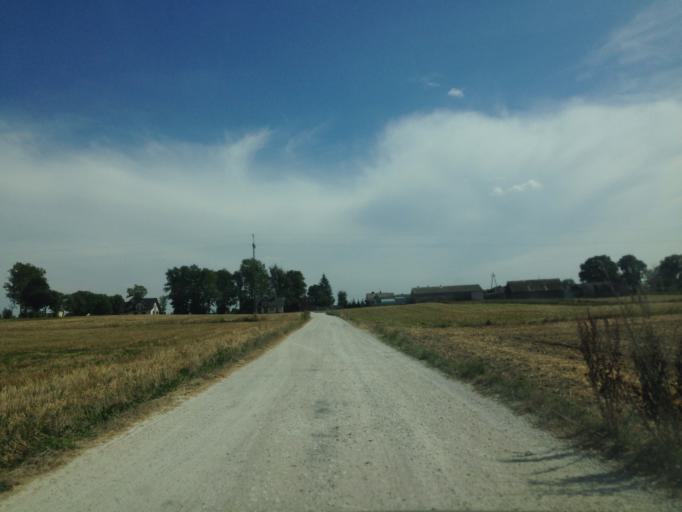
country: PL
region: Kujawsko-Pomorskie
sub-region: Powiat brodnicki
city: Bartniczka
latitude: 53.2299
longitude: 19.5958
